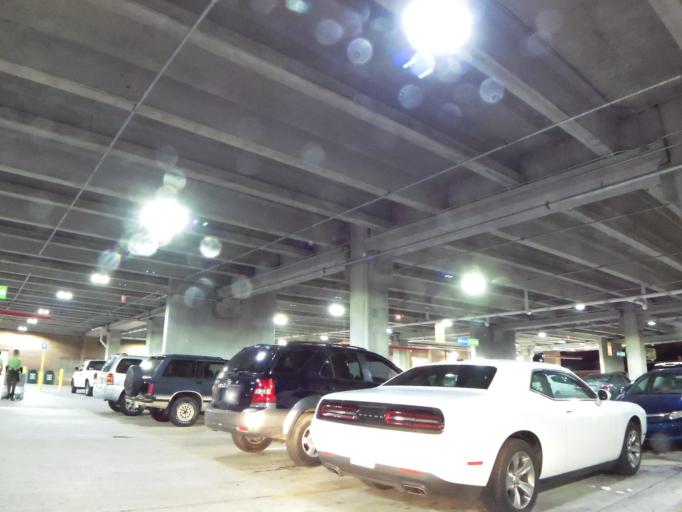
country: US
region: Tennessee
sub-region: Knox County
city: Knoxville
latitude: 35.9699
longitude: -83.9538
